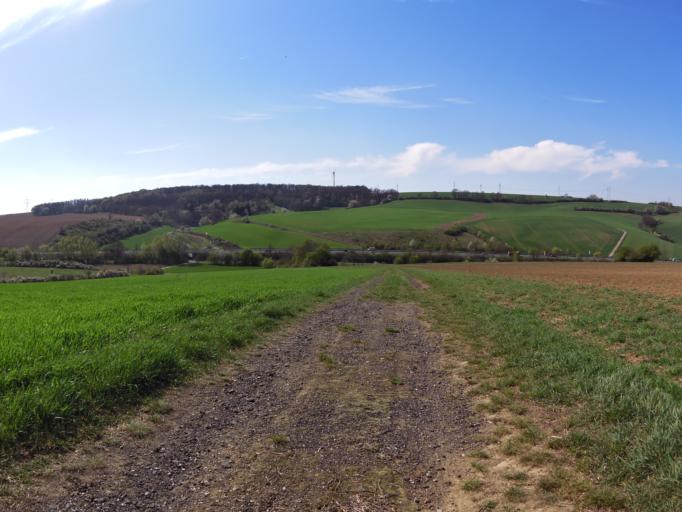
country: DE
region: Bavaria
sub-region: Regierungsbezirk Unterfranken
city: Rottendorf
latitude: 49.7862
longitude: 10.0408
